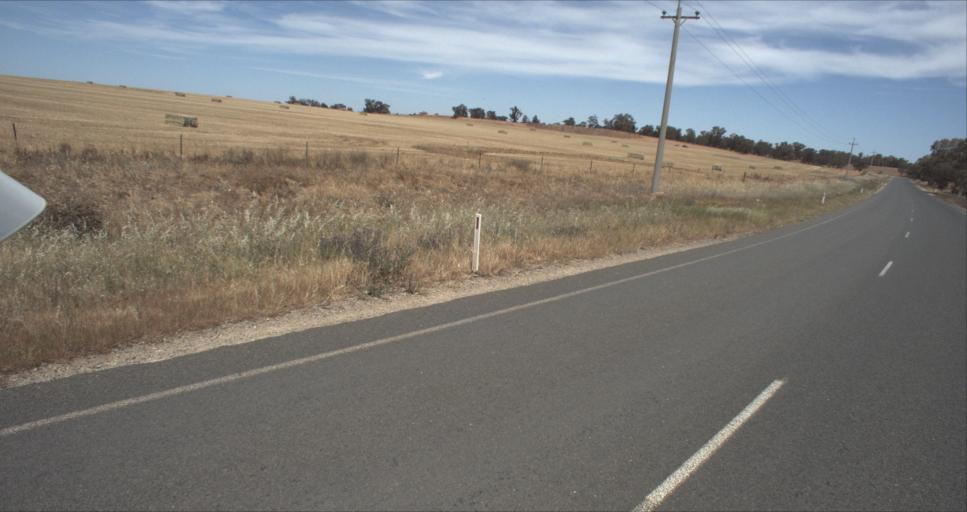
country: AU
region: New South Wales
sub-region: Leeton
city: Leeton
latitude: -34.6536
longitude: 146.4617
